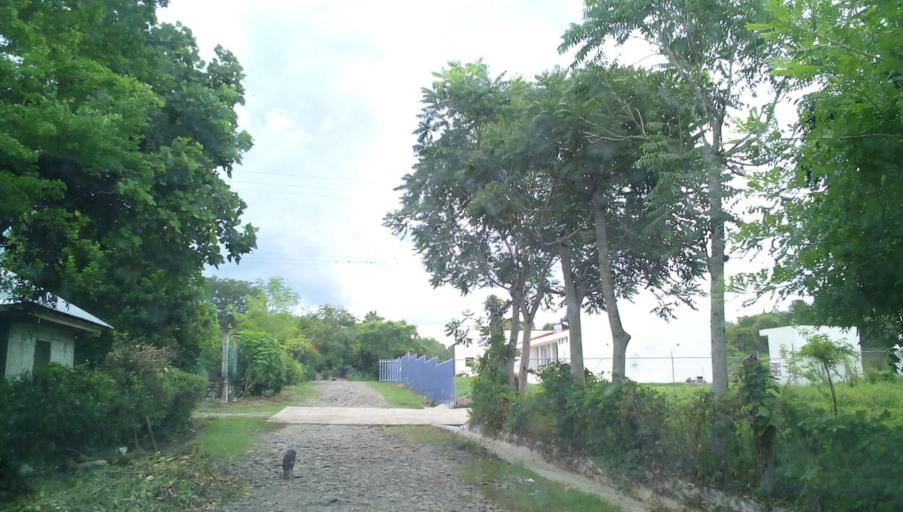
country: MX
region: Veracruz
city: Tepetzintla
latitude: 21.1289
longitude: -97.8566
